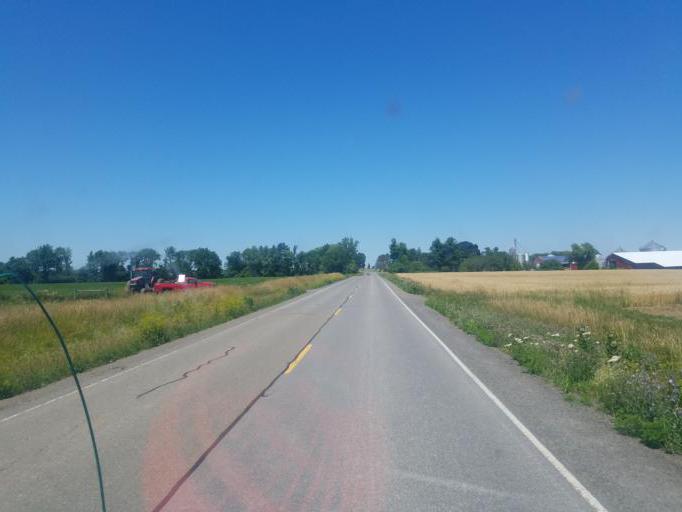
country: US
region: New York
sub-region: Yates County
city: Penn Yan
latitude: 42.6922
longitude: -77.0003
